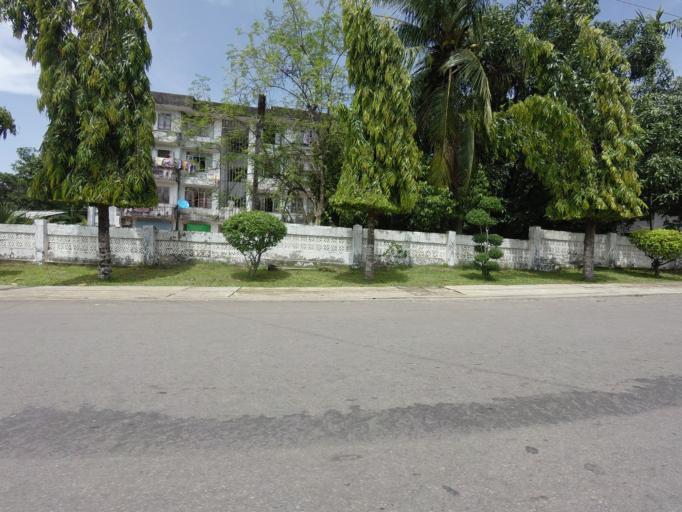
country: MM
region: Mon
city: Mawlamyine
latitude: 16.4620
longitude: 97.6279
